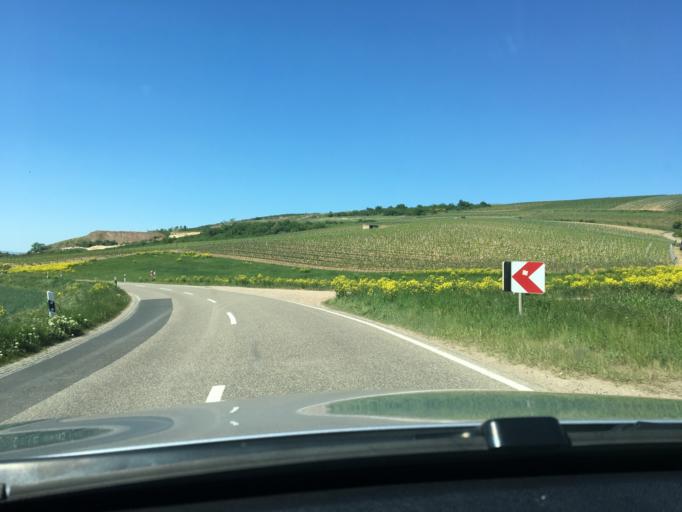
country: DE
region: Rheinland-Pfalz
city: Wendelsheim
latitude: 49.7782
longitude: 7.9927
